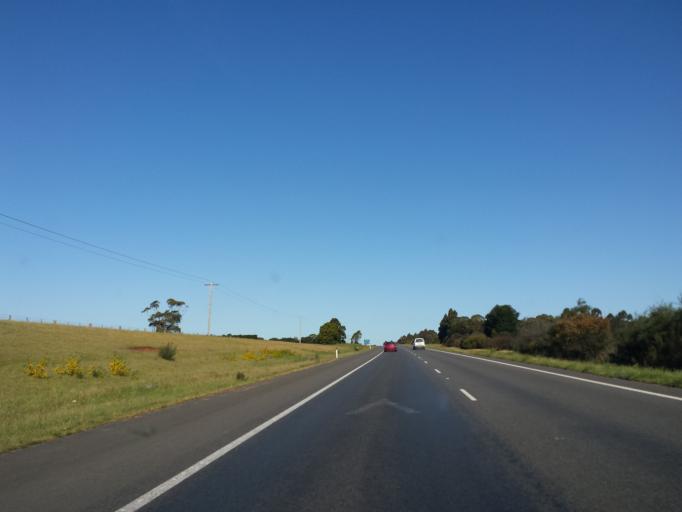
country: AU
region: Victoria
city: Brown Hill
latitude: -37.5593
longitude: 144.0857
